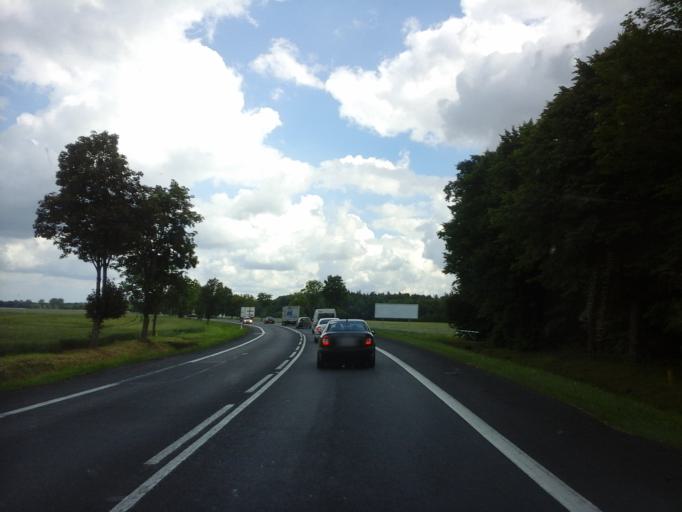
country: PL
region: West Pomeranian Voivodeship
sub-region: Powiat bialogardzki
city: Bialogard
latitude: 54.0815
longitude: 15.9794
